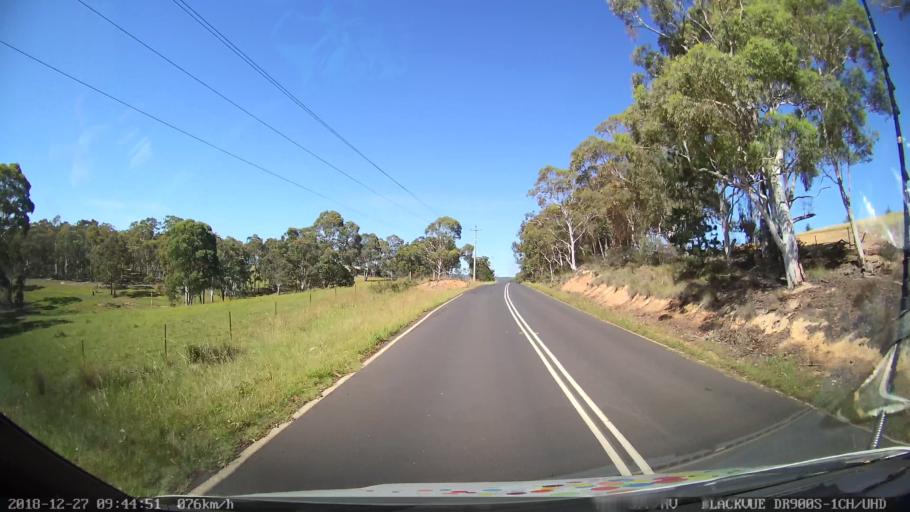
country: AU
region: New South Wales
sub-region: Lithgow
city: Portland
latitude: -33.3198
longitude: 149.9900
